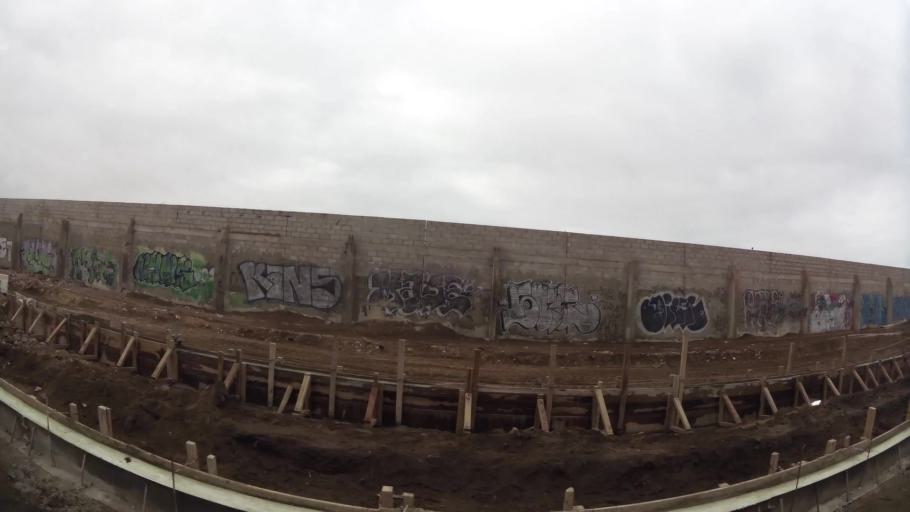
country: PE
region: Lima
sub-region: Lima
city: Surco
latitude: -12.2122
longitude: -77.0159
